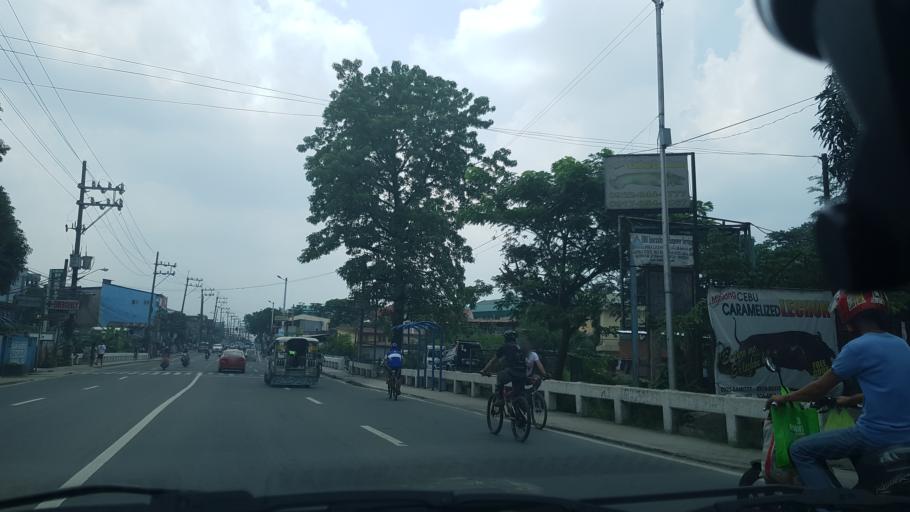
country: PH
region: Calabarzon
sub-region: Province of Rizal
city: San Mateo
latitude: 14.6745
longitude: 121.1097
